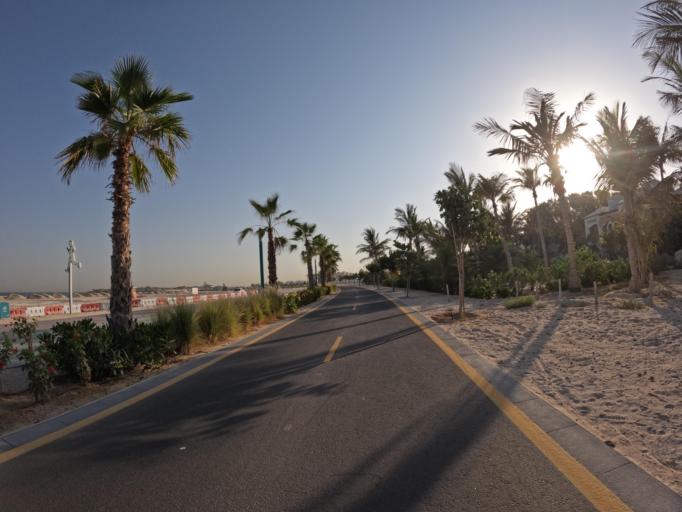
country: AE
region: Dubai
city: Dubai
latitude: 25.1882
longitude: 55.2274
